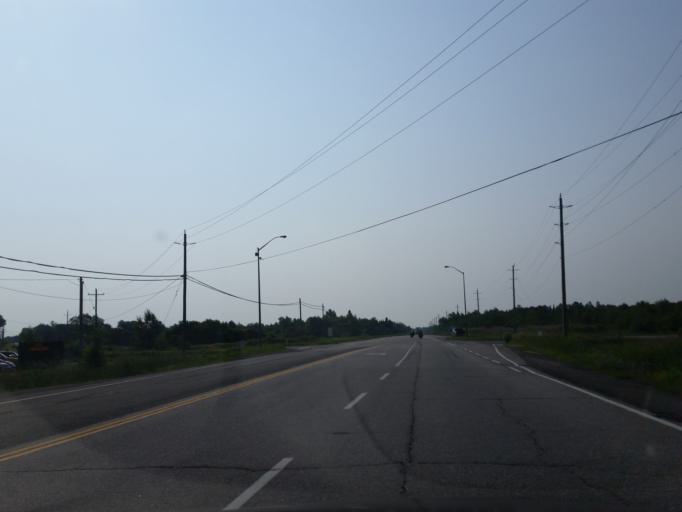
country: CA
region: Ontario
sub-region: Nipissing District
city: North Bay
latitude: 46.3784
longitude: -79.9744
